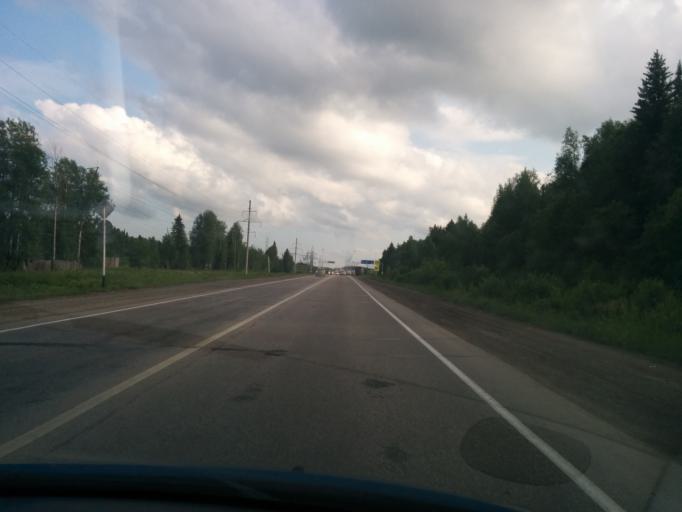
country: RU
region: Perm
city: Novyye Lyady
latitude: 58.0559
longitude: 56.4280
